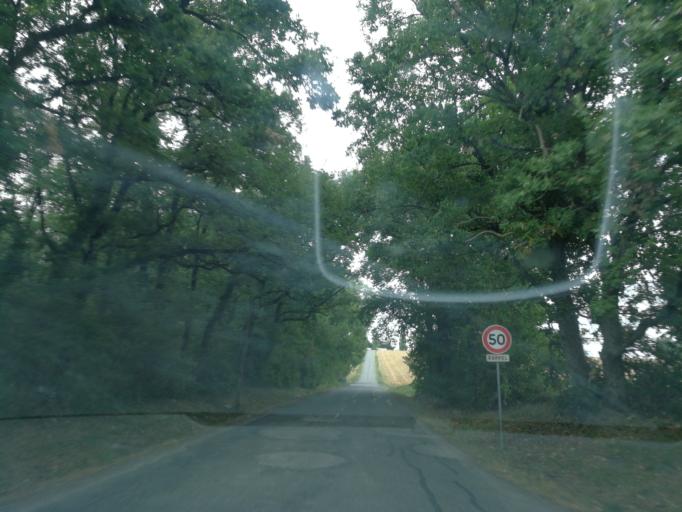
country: FR
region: Midi-Pyrenees
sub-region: Departement de la Haute-Garonne
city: Flourens
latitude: 43.6056
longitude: 1.5369
